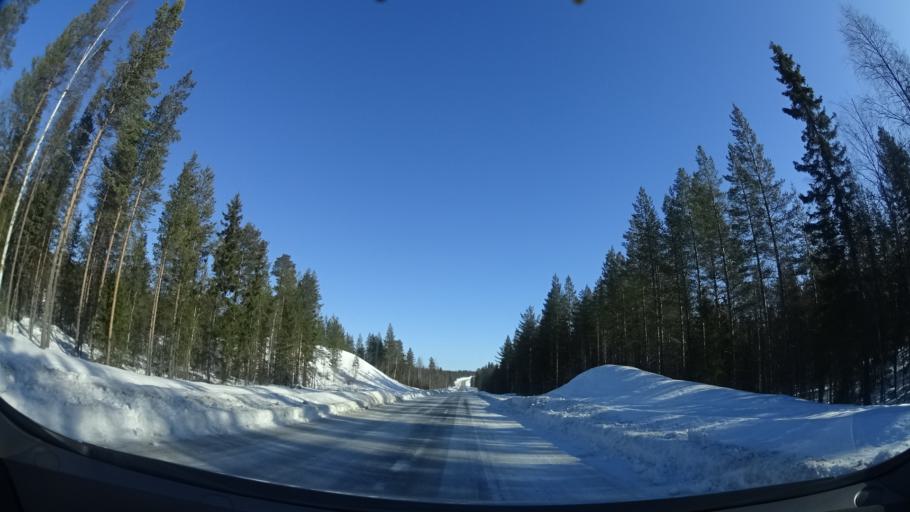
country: SE
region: Vaesterbotten
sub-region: Skelleftea Kommun
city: Langsele
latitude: 65.1282
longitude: 20.1311
